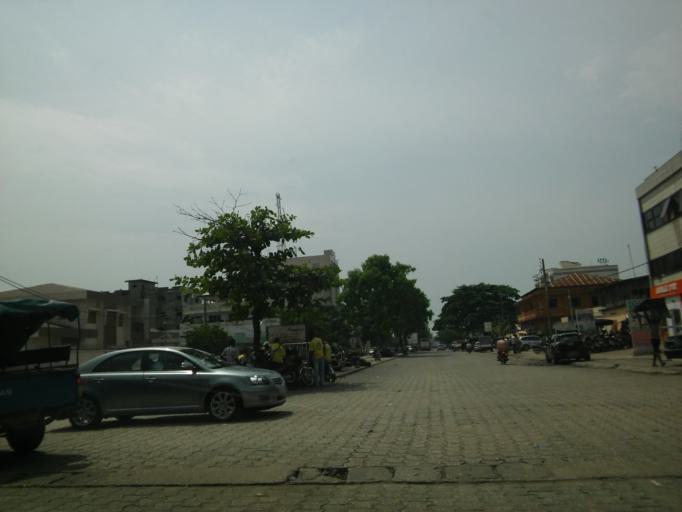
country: BJ
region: Littoral
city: Cotonou
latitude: 6.3600
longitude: 2.4291
